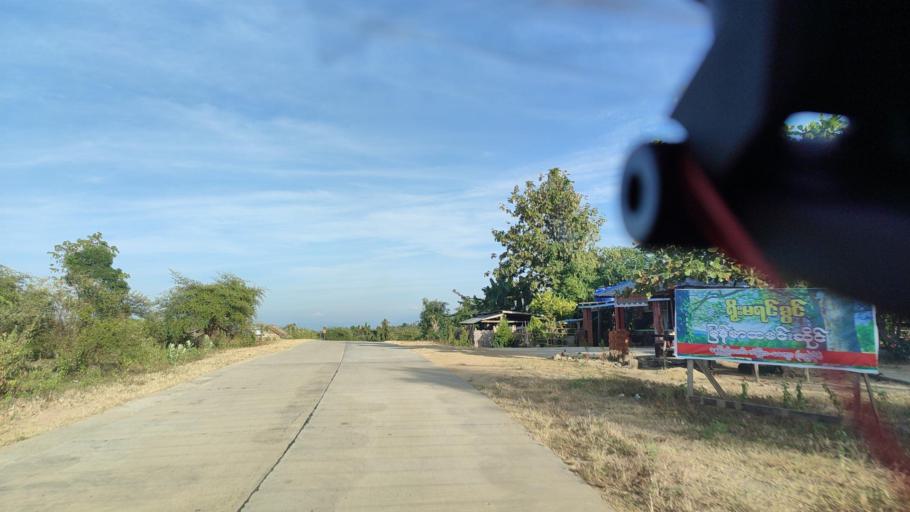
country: MM
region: Magway
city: Taungdwingyi
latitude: 20.0182
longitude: 95.8023
